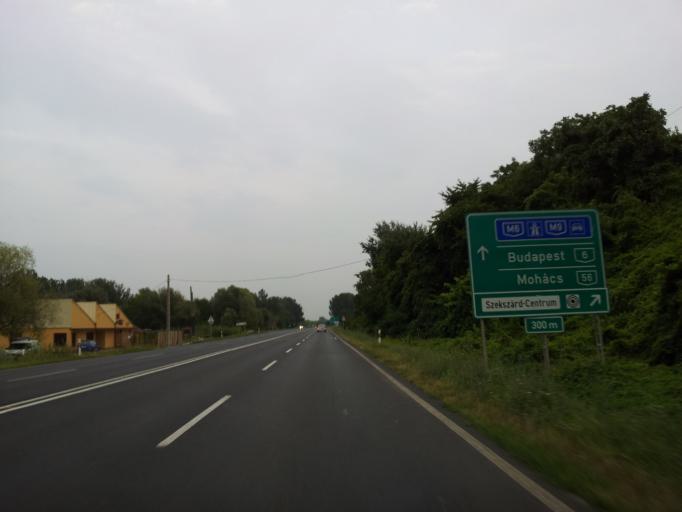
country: HU
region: Tolna
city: Szekszard
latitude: 46.3798
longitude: 18.6998
